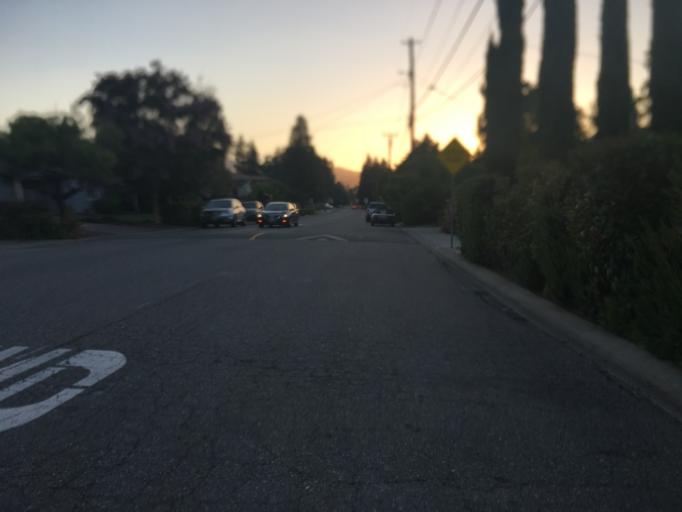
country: US
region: California
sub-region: Santa Clara County
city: Cupertino
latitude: 37.3254
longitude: -122.0395
